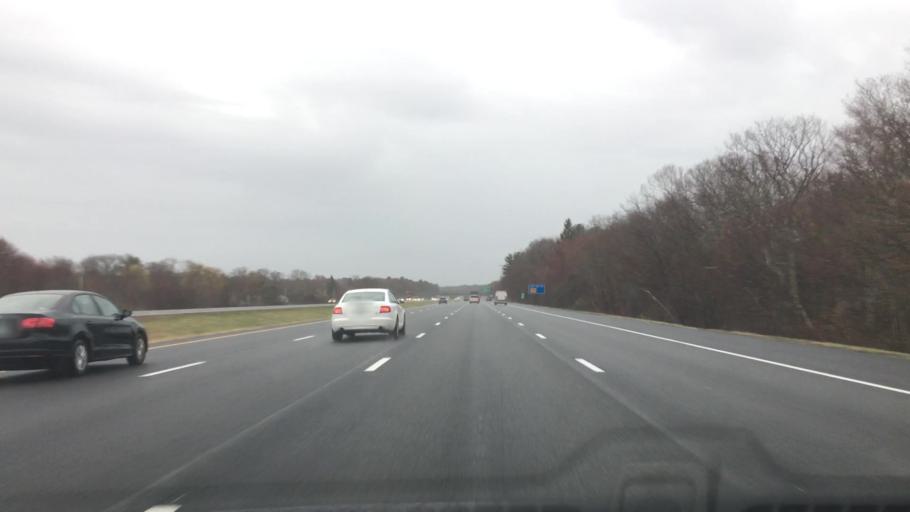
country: US
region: Massachusetts
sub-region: Essex County
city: West Newbury
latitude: 42.7641
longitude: -70.9371
